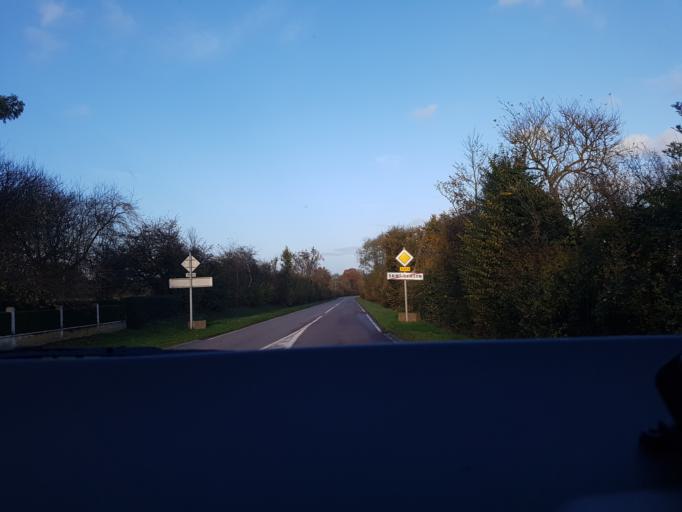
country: FR
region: Lower Normandy
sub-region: Departement du Calvados
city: Troarn
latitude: 49.1864
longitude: -0.1571
